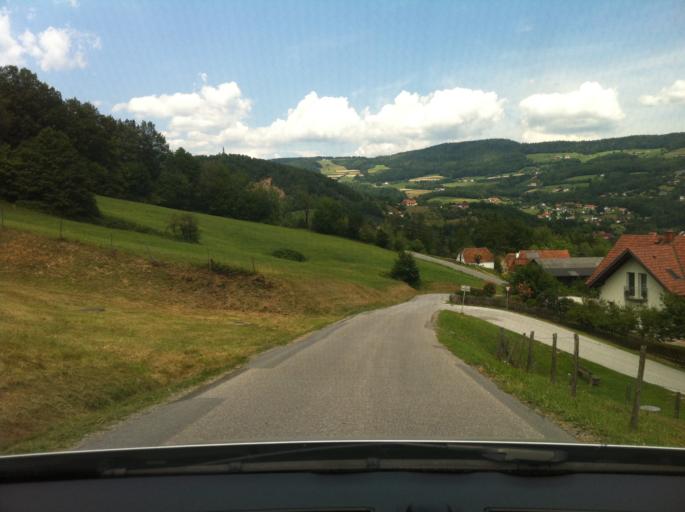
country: AT
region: Styria
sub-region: Politischer Bezirk Hartberg-Fuerstenfeld
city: Stubenberg
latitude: 47.2356
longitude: 15.7893
